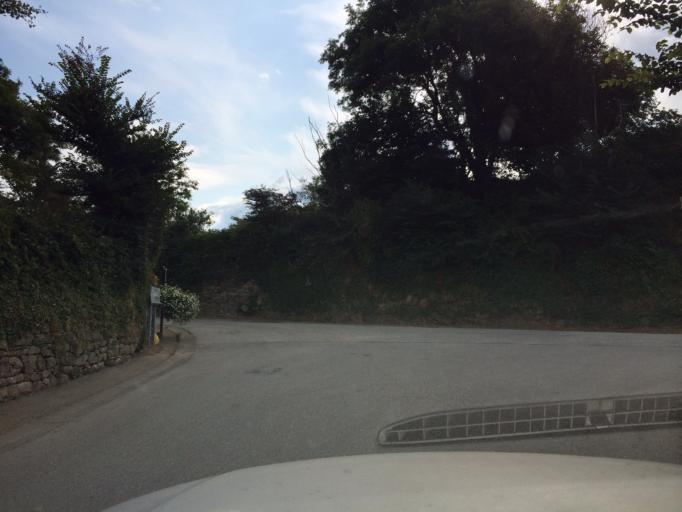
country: FR
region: Lower Normandy
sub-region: Departement de la Manche
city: Beaumont-Hague
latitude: 49.6972
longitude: -1.8604
